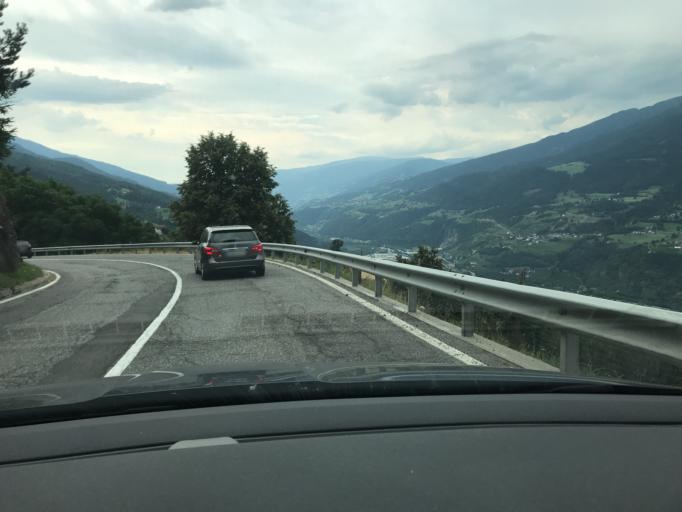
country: IT
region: Trentino-Alto Adige
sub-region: Bolzano
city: Bressanone
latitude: 46.6996
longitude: 11.6746
